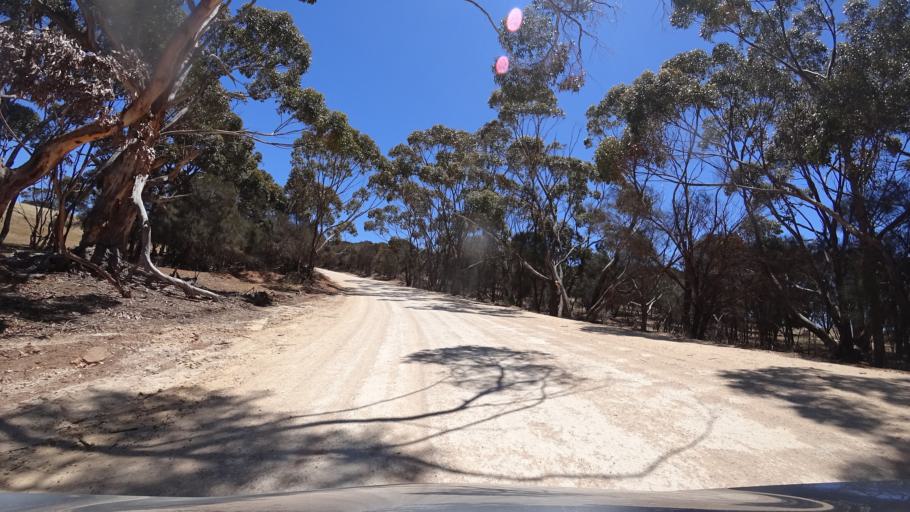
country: AU
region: South Australia
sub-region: Kangaroo Island
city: Kingscote
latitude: -35.6286
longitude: 137.2019
